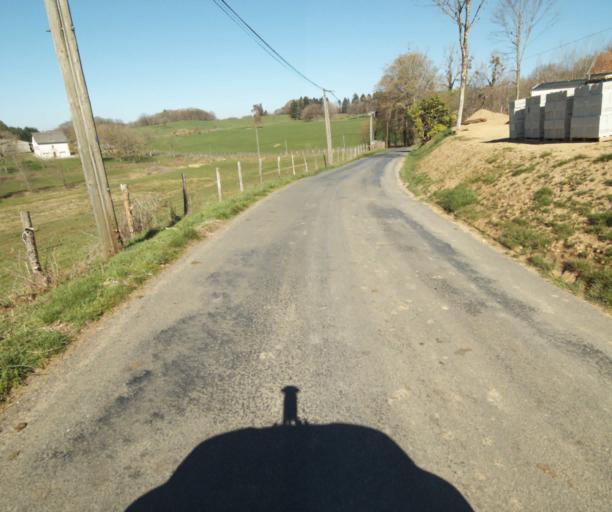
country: FR
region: Limousin
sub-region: Departement de la Correze
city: Saint-Clement
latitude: 45.3500
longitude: 1.6580
